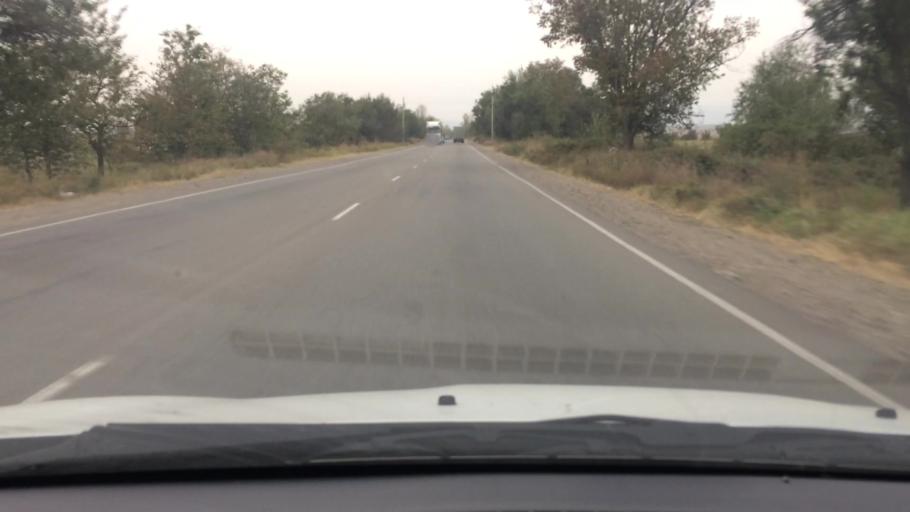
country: GE
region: Kvemo Kartli
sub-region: Marneuli
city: Marneuli
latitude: 41.5628
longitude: 44.7756
